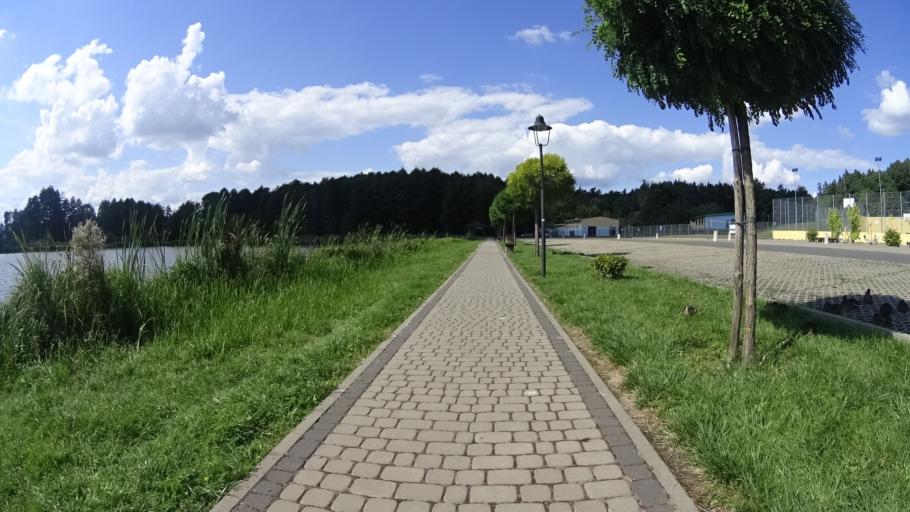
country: PL
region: Masovian Voivodeship
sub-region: Powiat grojecki
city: Mogielnica
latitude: 51.6978
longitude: 20.7247
